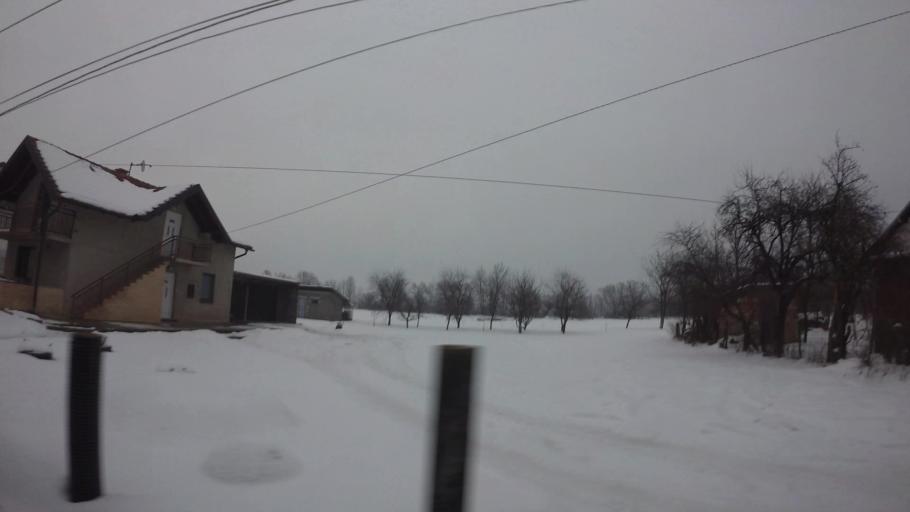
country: BA
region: Federation of Bosnia and Herzegovina
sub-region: Kanton Sarajevo
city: Sarajevo
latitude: 43.8442
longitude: 18.2979
